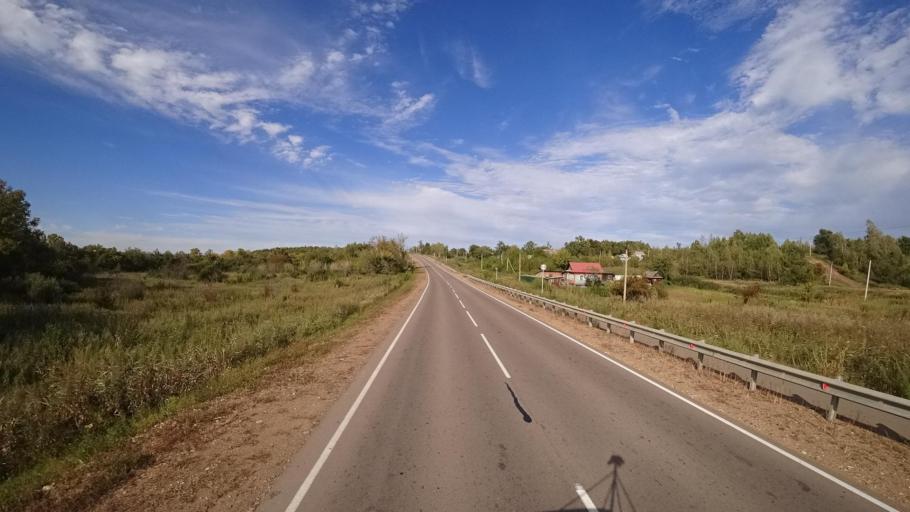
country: RU
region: Primorskiy
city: Dostoyevka
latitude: 44.2964
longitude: 133.4444
